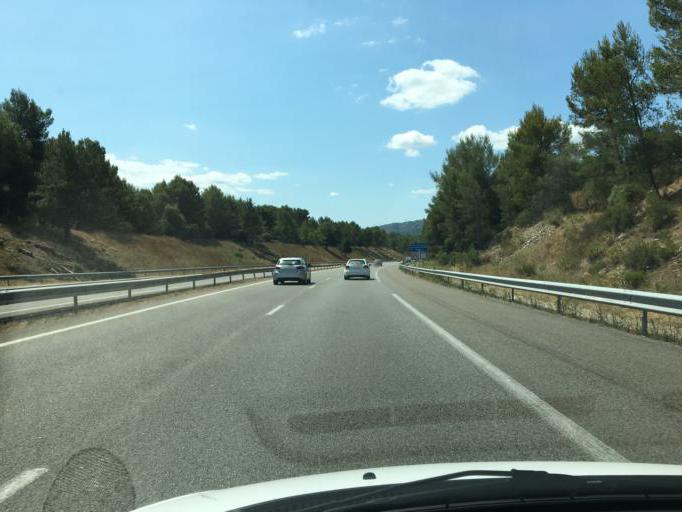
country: FR
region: Provence-Alpes-Cote d'Azur
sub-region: Departement des Bouches-du-Rhone
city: Belcodene
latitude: 43.4133
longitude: 5.5789
